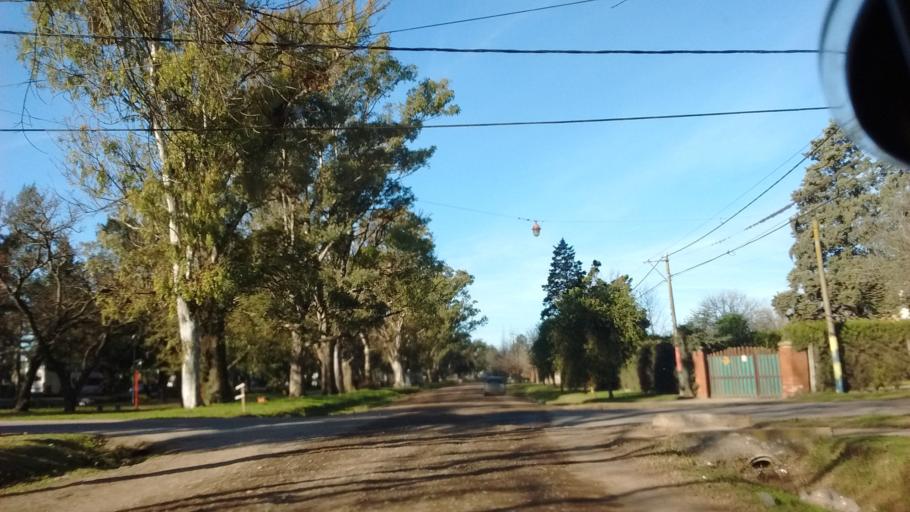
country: AR
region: Santa Fe
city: Funes
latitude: -32.9232
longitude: -60.8051
